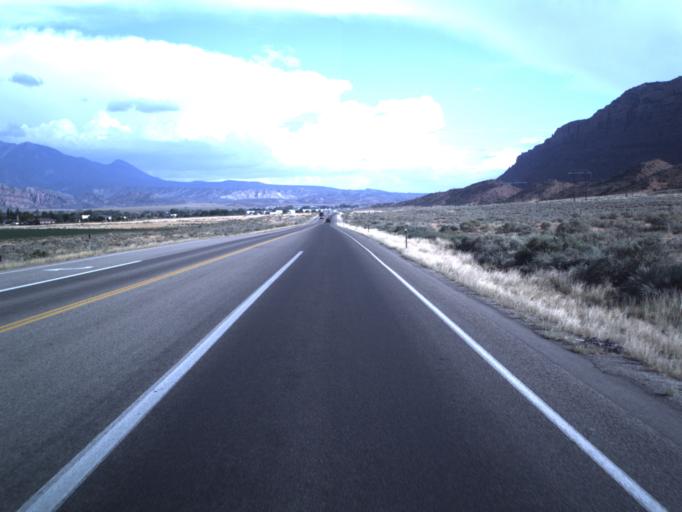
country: US
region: Utah
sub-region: Grand County
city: Moab
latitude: 38.5109
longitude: -109.4863
